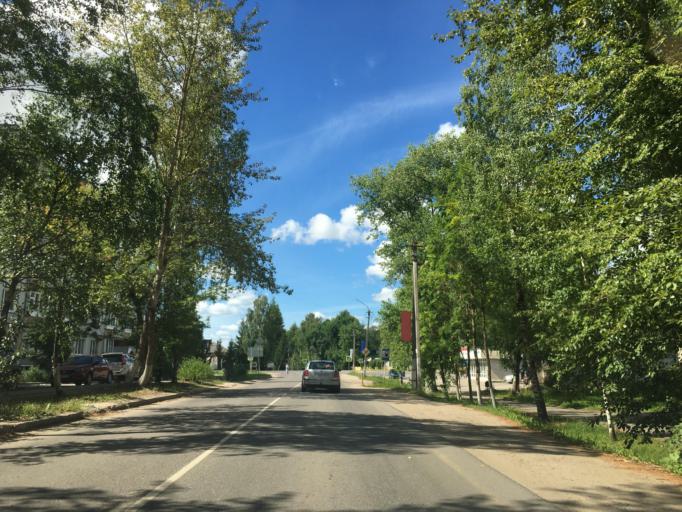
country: RU
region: Pskov
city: Palkino
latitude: 57.5409
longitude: 28.0108
